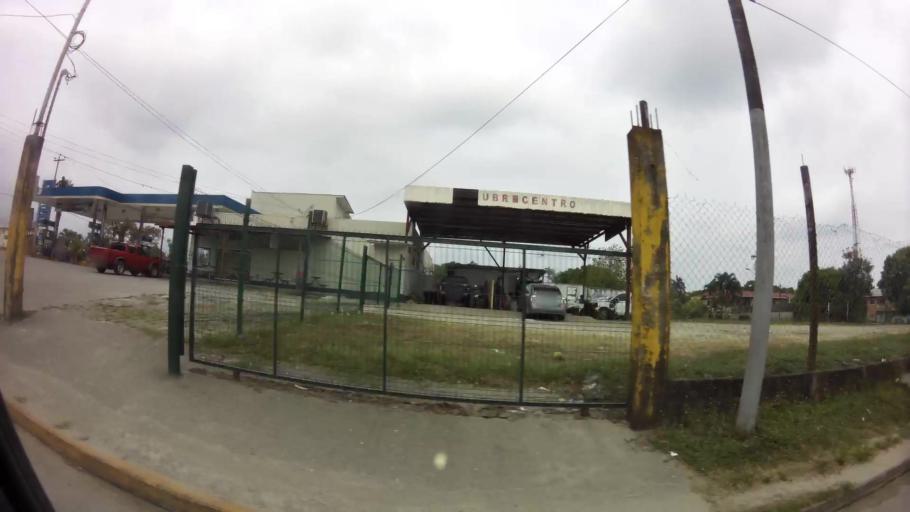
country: HN
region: Atlantida
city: Tela
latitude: 15.7627
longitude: -87.4797
